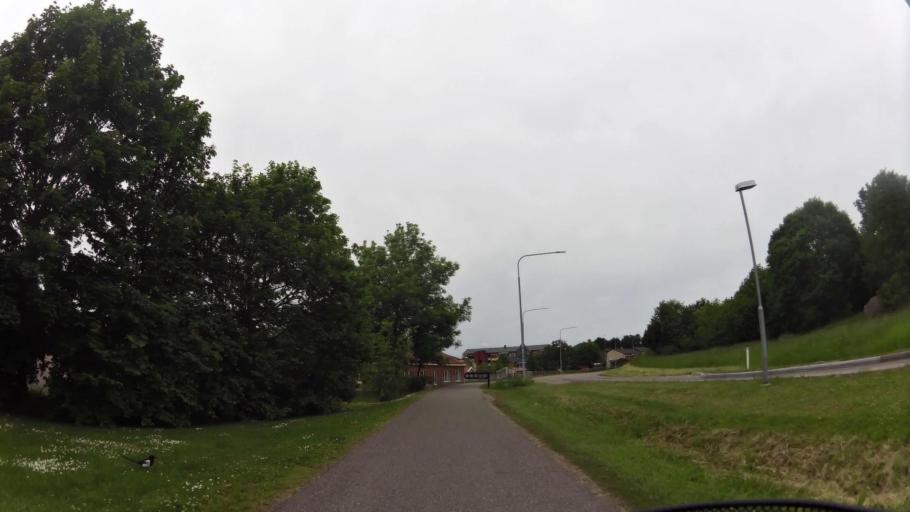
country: SE
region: OEstergoetland
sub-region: Linkopings Kommun
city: Linkoping
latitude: 58.3849
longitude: 15.5723
